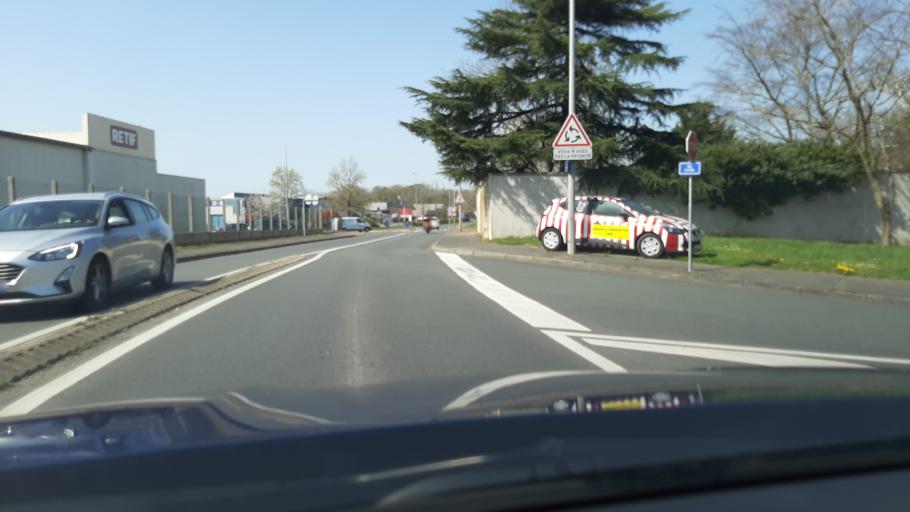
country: FR
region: Pays de la Loire
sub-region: Departement de Maine-et-Loire
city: Angers
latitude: 47.4825
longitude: -0.5020
